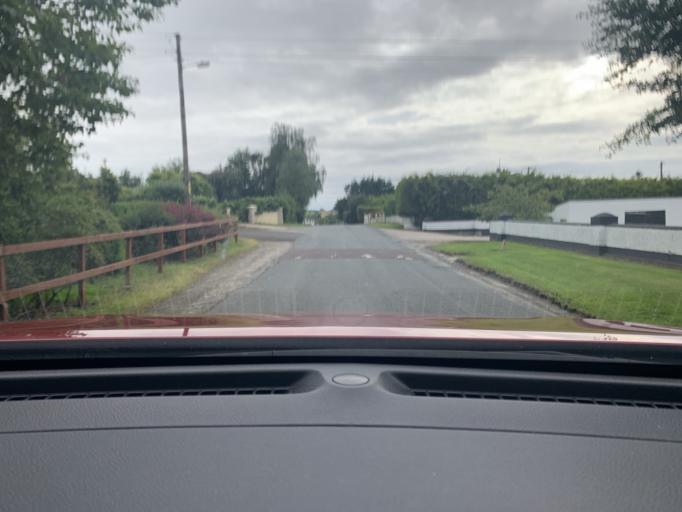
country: IE
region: Ulster
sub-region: County Donegal
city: Letterkenny
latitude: 54.9444
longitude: -7.6798
